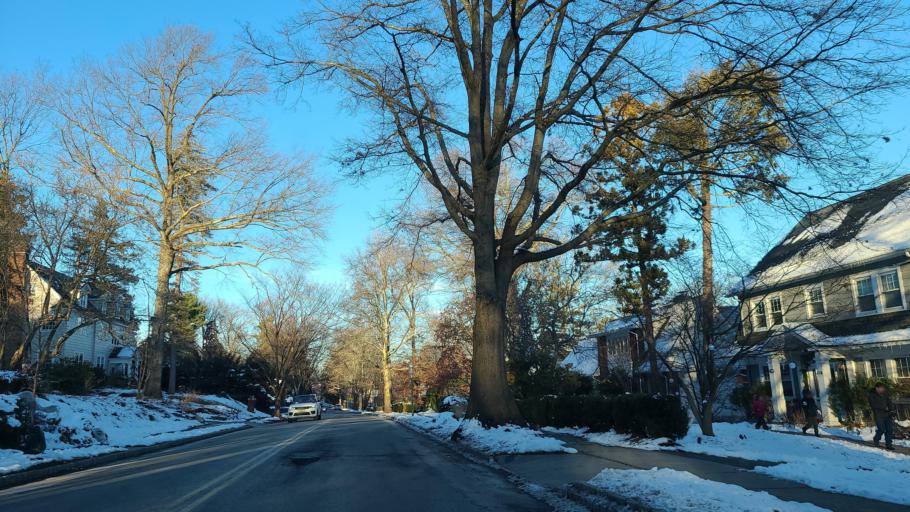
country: US
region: New Jersey
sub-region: Essex County
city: South Orange
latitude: 40.7562
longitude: -74.2590
